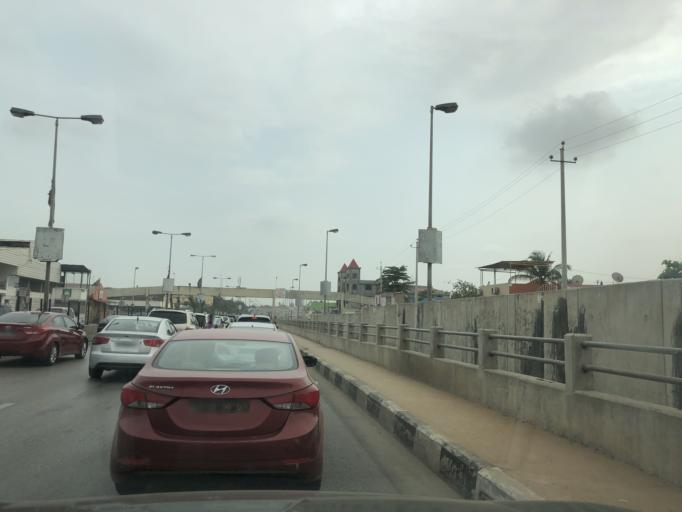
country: AO
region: Luanda
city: Luanda
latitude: -8.8530
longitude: 13.2088
